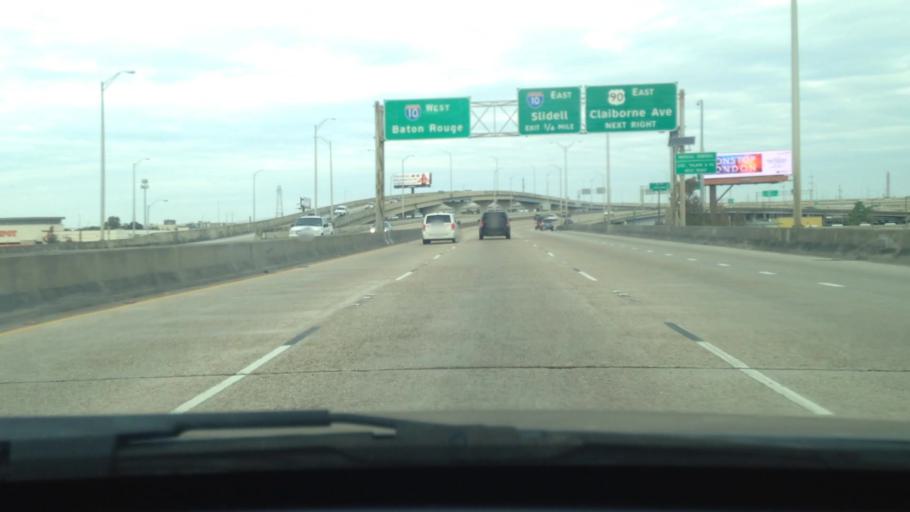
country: US
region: Louisiana
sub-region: Orleans Parish
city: New Orleans
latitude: 29.9475
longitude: -90.0823
